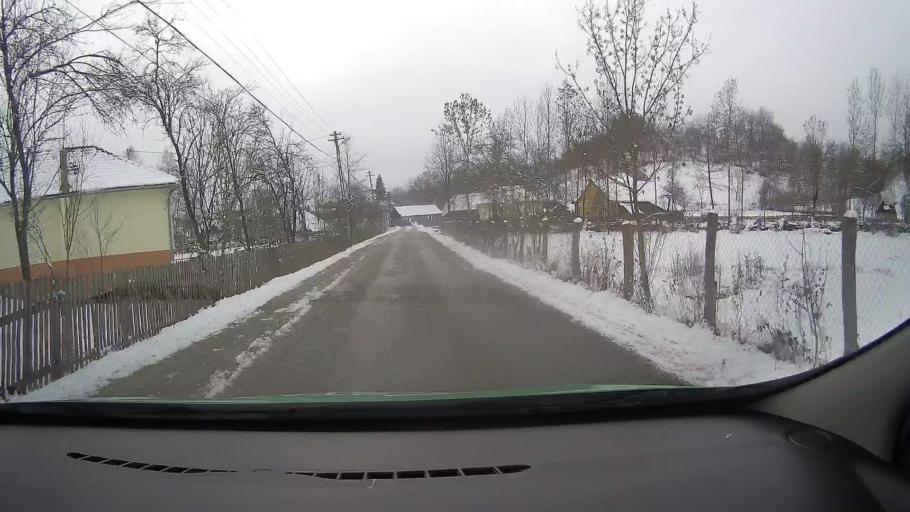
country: RO
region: Alba
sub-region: Comuna Almasu Mare
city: Almasu Mare
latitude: 46.0928
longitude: 23.1309
